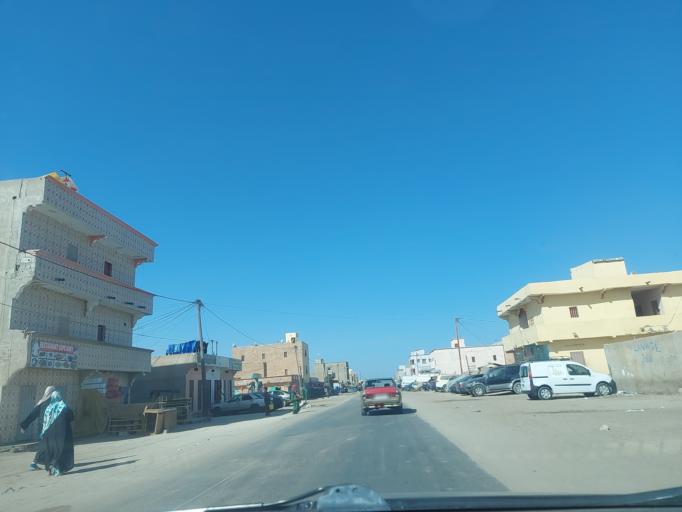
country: MR
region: Nouakchott
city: Nouakchott
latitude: 18.0638
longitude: -16.0016
